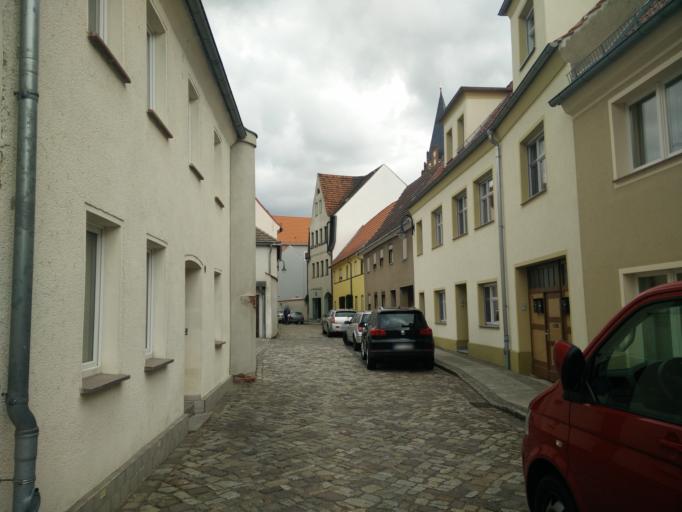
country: DE
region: Brandenburg
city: Bad Liebenwerda
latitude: 51.5150
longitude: 13.3915
